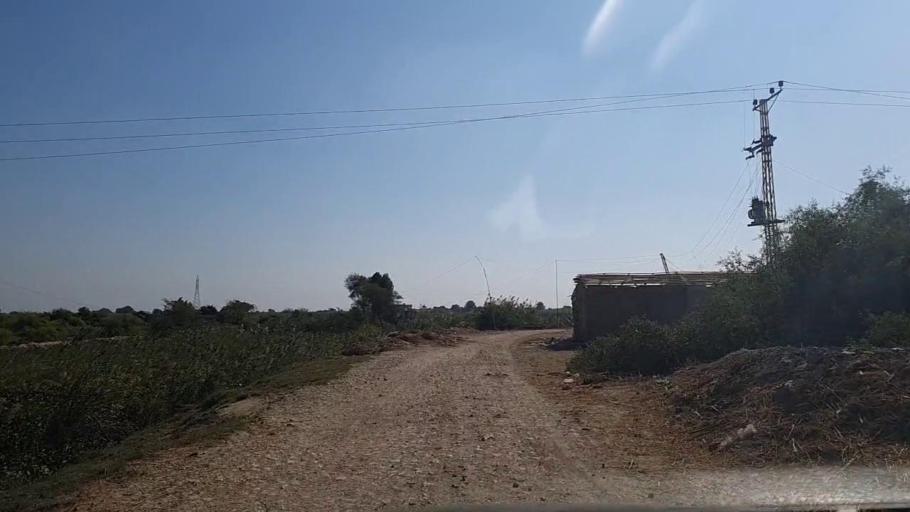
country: PK
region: Sindh
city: Mirpur Batoro
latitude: 24.6904
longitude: 68.1854
